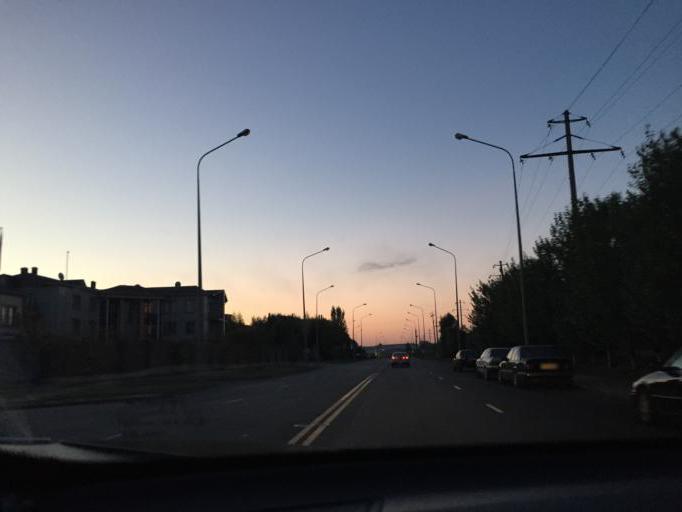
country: KZ
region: Astana Qalasy
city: Astana
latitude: 51.1436
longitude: 71.4532
